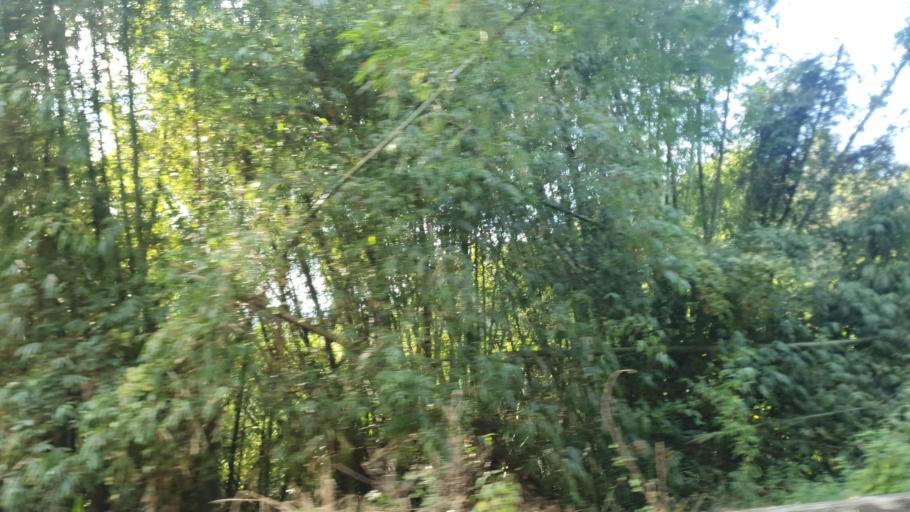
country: TW
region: Taiwan
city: Yujing
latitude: 23.0424
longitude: 120.3971
